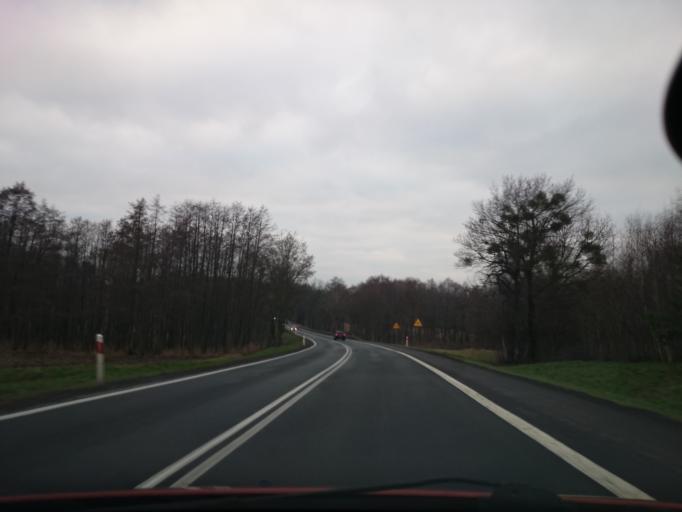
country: PL
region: Opole Voivodeship
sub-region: Powiat opolski
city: Niemodlin
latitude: 50.6329
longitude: 17.5935
